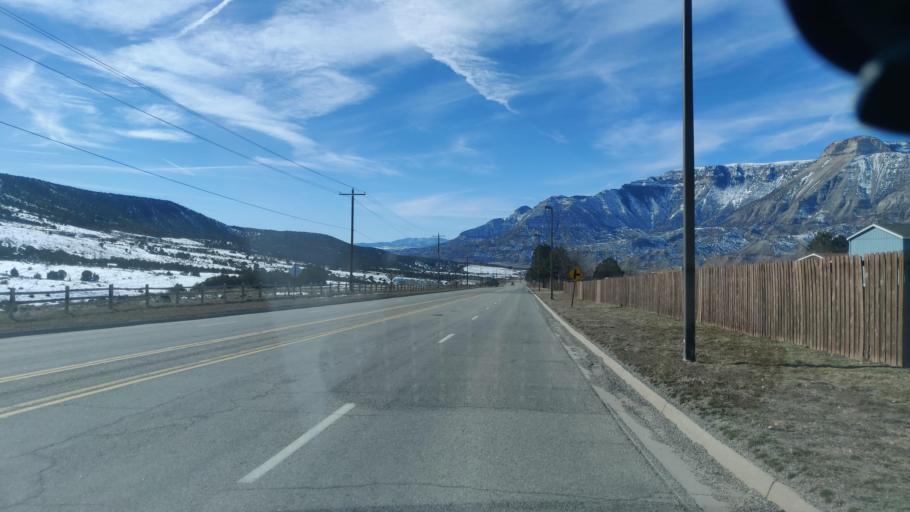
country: US
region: Colorado
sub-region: Garfield County
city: Battlement Mesa
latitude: 39.4255
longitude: -108.0364
